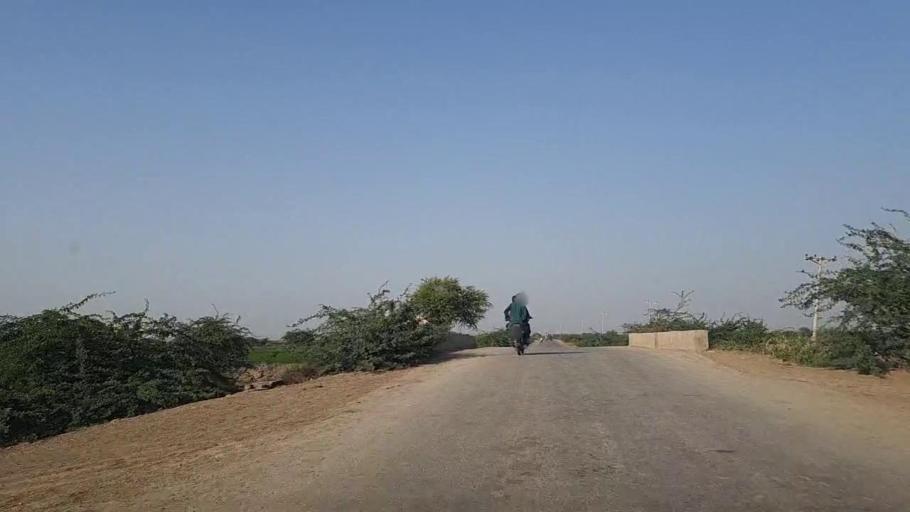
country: PK
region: Sindh
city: Mirpur Batoro
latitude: 24.5989
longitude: 68.4003
